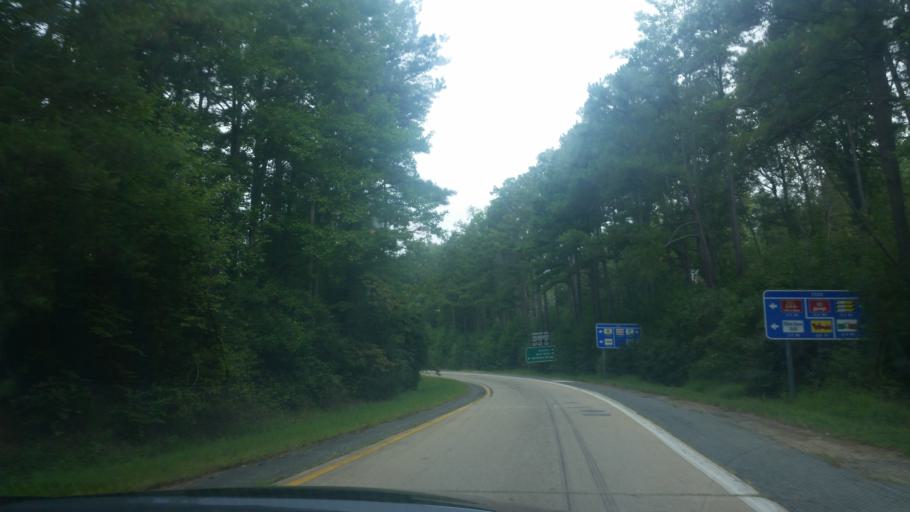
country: US
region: Virginia
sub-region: Henrico County
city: Sandston
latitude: 37.5169
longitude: -77.1868
